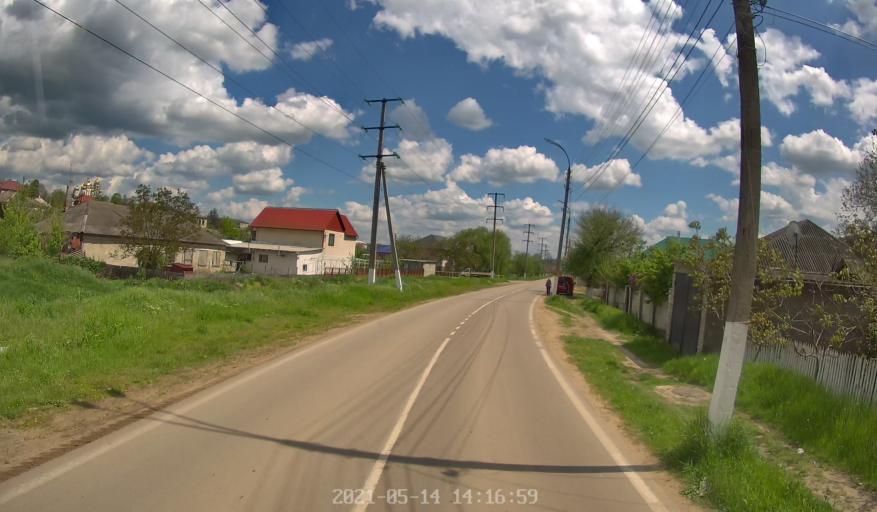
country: MD
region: Hincesti
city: Hincesti
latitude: 46.8241
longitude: 28.5900
